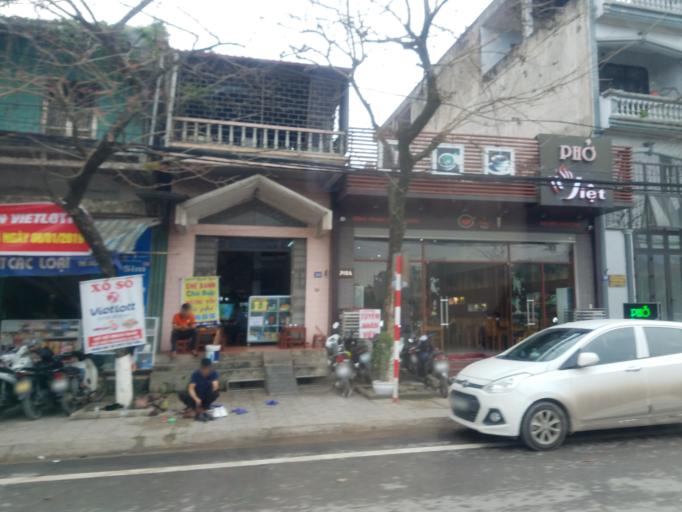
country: VN
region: Thai Nguyen
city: Thanh Pho Thai Nguyen
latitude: 21.5830
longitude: 105.8386
